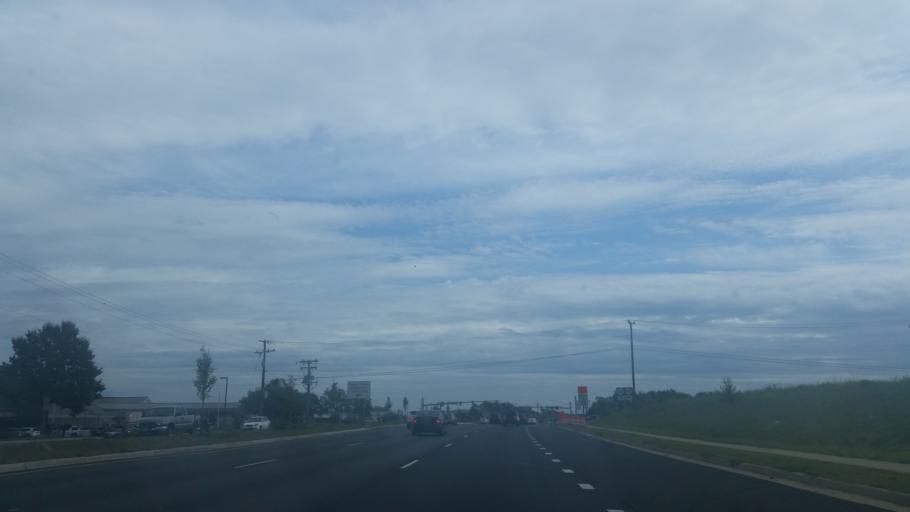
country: US
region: Virginia
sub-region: Stafford County
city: Falmouth
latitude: 38.3558
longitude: -77.5127
